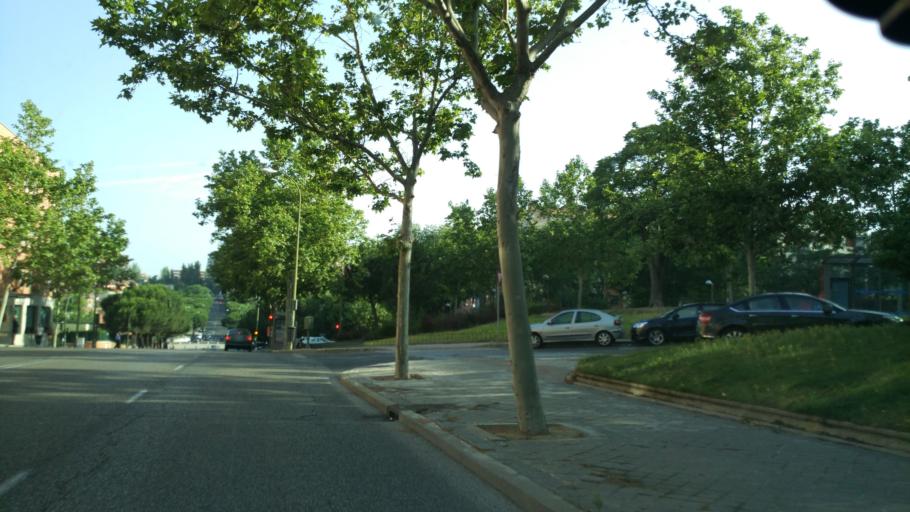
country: ES
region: Madrid
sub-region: Provincia de Madrid
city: Tetuan de las Victorias
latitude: 40.4735
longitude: -3.7206
